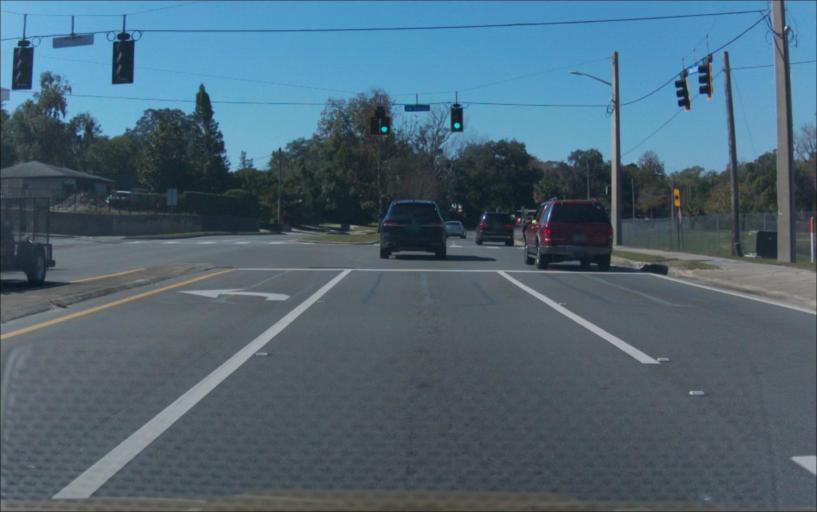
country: US
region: Florida
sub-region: Orange County
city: Winter Park
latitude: 28.6258
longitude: -81.3291
